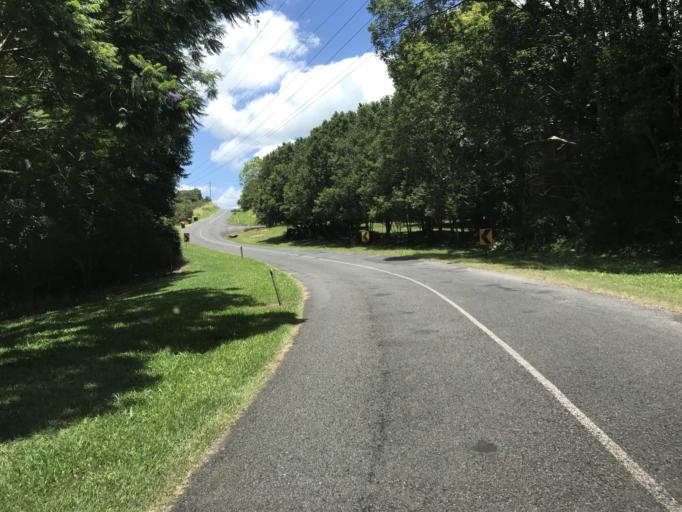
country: AU
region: Queensland
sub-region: Tablelands
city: Atherton
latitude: -17.3443
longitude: 145.5947
